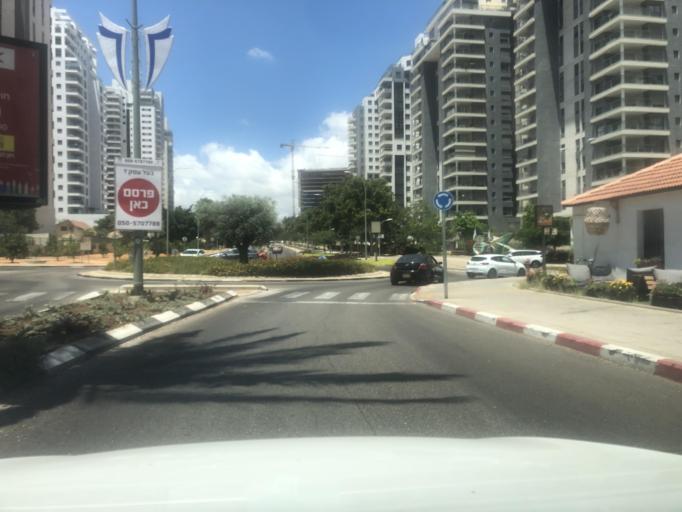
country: IL
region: Central District
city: Hod HaSharon
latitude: 32.1640
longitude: 34.9022
